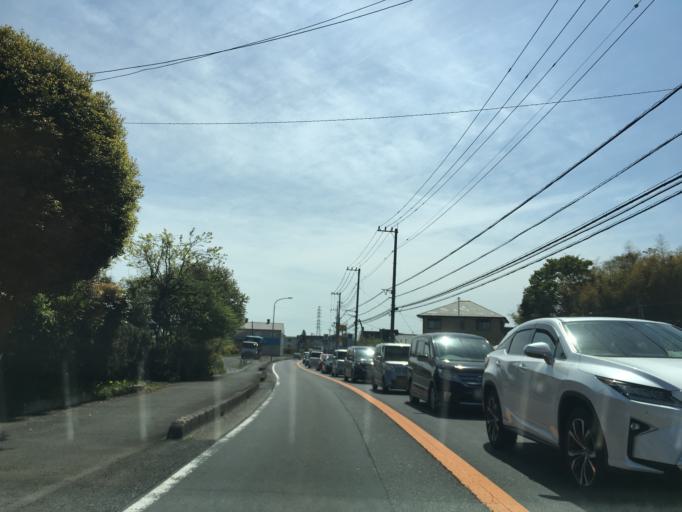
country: JP
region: Saitama
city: Sugito
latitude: 36.0047
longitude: 139.7025
